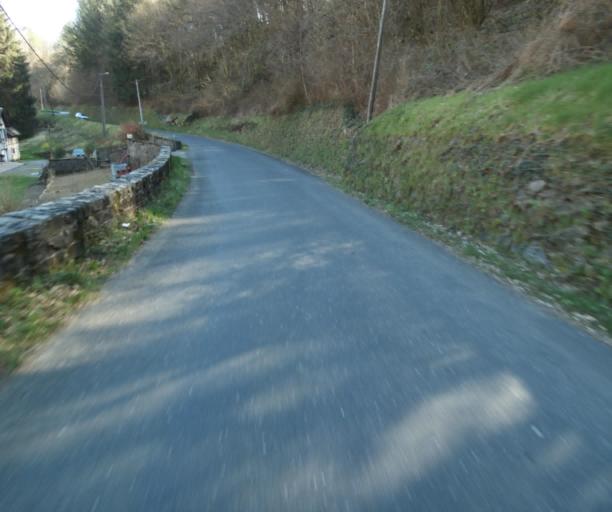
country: FR
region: Limousin
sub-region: Departement de la Correze
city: Tulle
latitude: 45.2730
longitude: 1.7380
